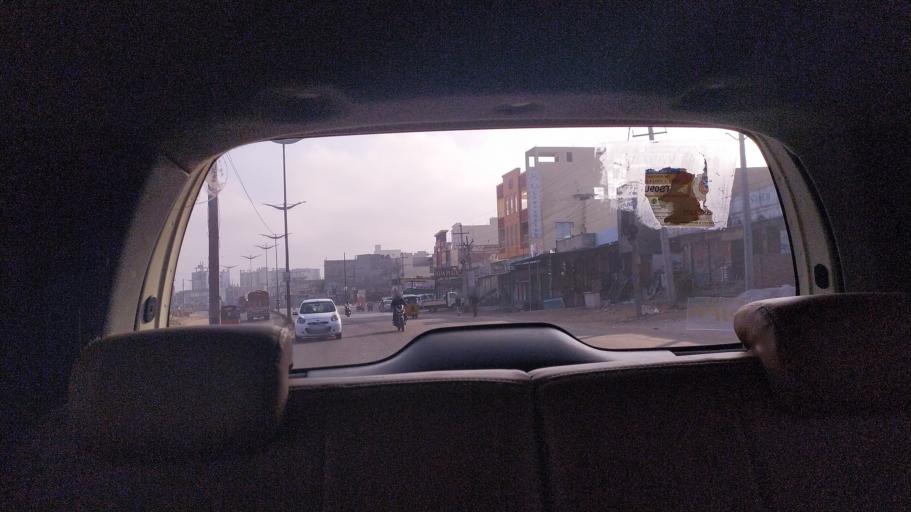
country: IN
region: Telangana
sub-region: Rangareddi
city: Balapur
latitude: 17.3144
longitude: 78.4632
